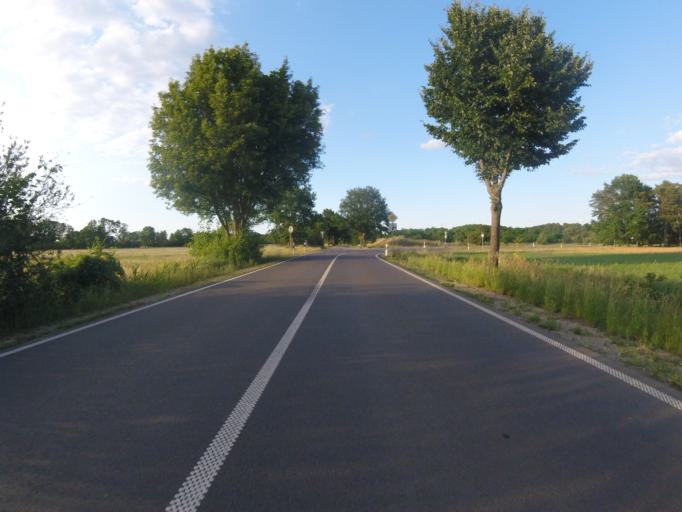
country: DE
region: Brandenburg
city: Mittenwalde
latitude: 52.2393
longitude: 13.5539
